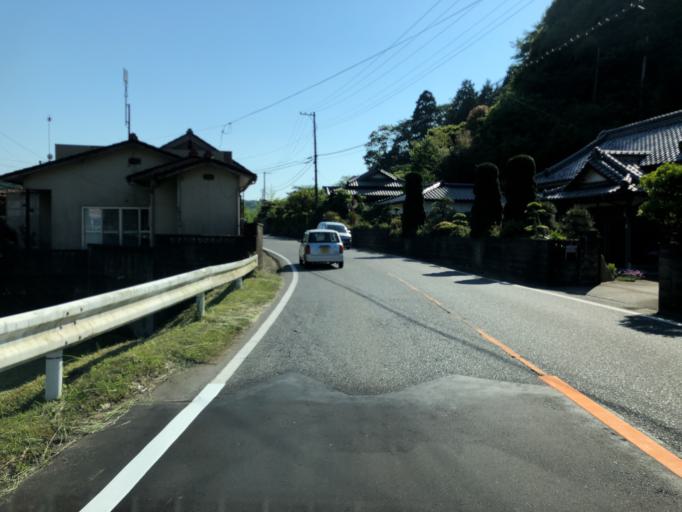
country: JP
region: Fukushima
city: Iwaki
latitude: 36.9435
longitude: 140.8203
